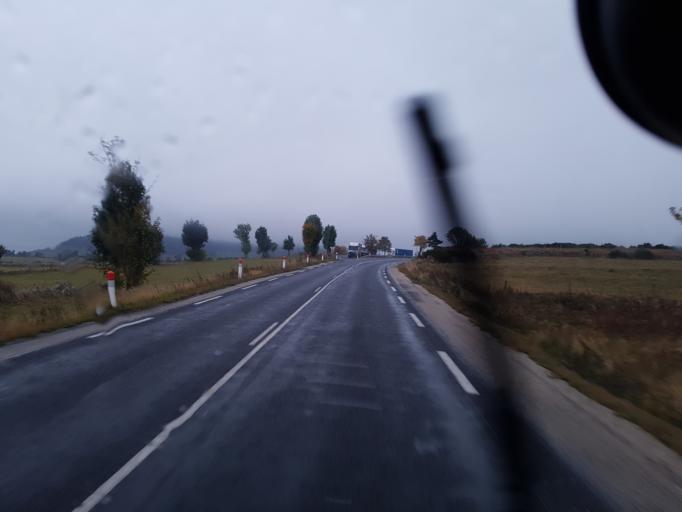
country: FR
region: Languedoc-Roussillon
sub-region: Departement de la Lozere
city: Langogne
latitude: 44.8427
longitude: 3.8585
